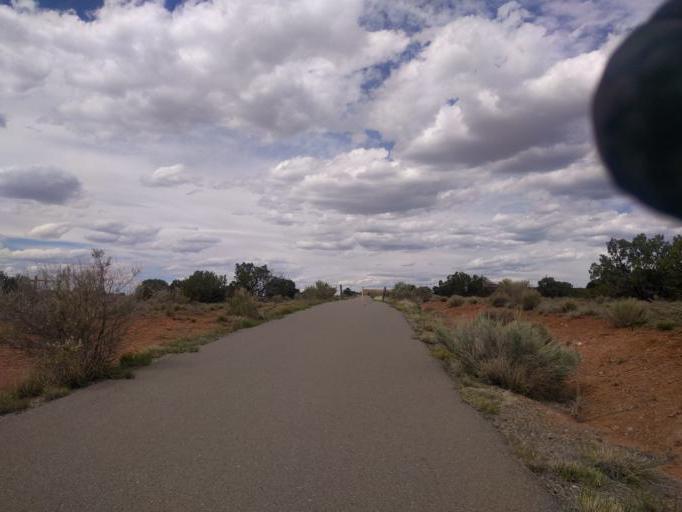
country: US
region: New Mexico
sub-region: Santa Fe County
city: Agua Fria
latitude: 35.5995
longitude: -106.0016
